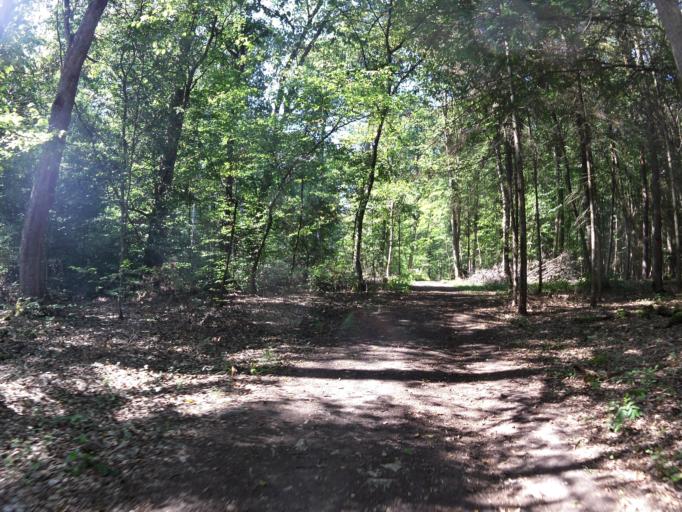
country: DE
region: Bavaria
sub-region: Regierungsbezirk Unterfranken
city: Gadheim
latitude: 49.8537
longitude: 9.8932
